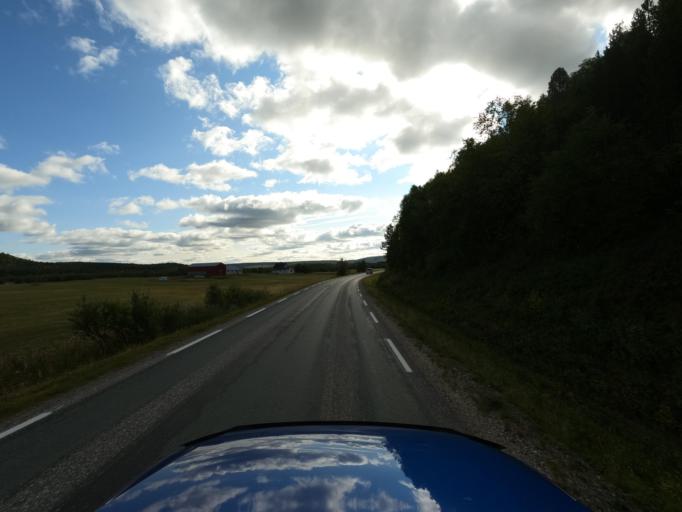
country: NO
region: Finnmark Fylke
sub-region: Karasjok
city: Karasjohka
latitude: 69.4122
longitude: 25.8036
